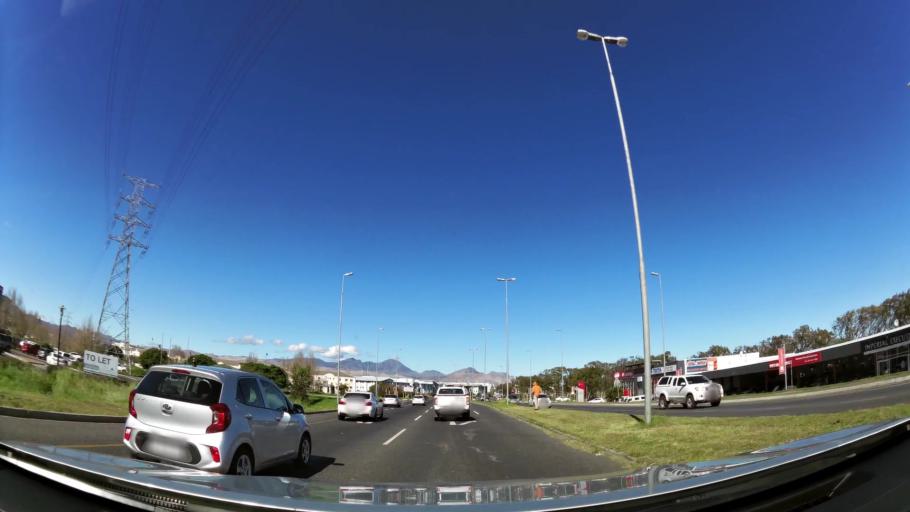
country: ZA
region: Western Cape
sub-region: Cape Winelands District Municipality
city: Stellenbosch
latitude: -34.0838
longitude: 18.8197
